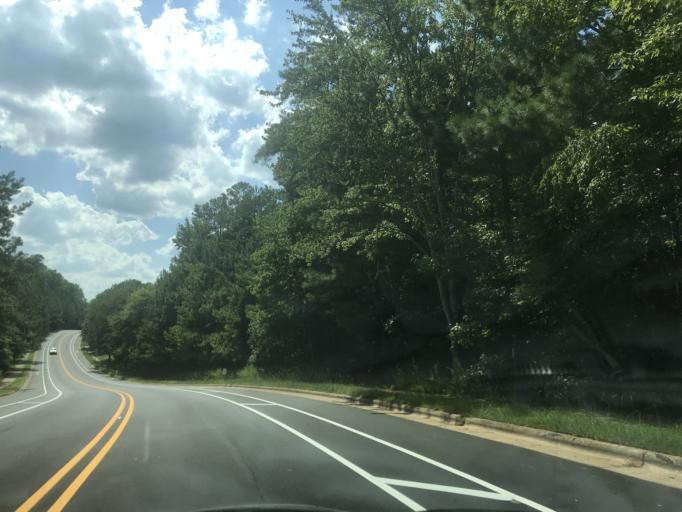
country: US
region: North Carolina
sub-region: Wake County
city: West Raleigh
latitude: 35.8864
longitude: -78.7144
